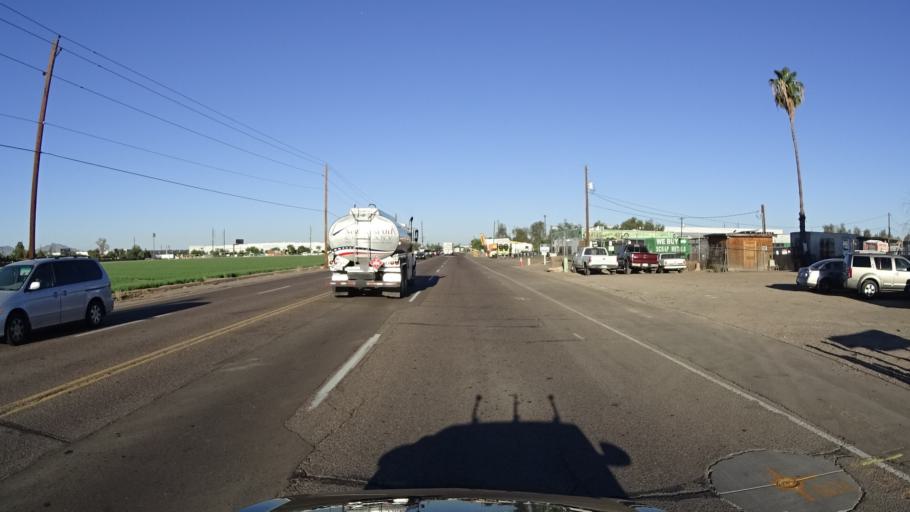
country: US
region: Arizona
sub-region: Maricopa County
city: Tolleson
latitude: 33.4372
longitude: -112.1998
